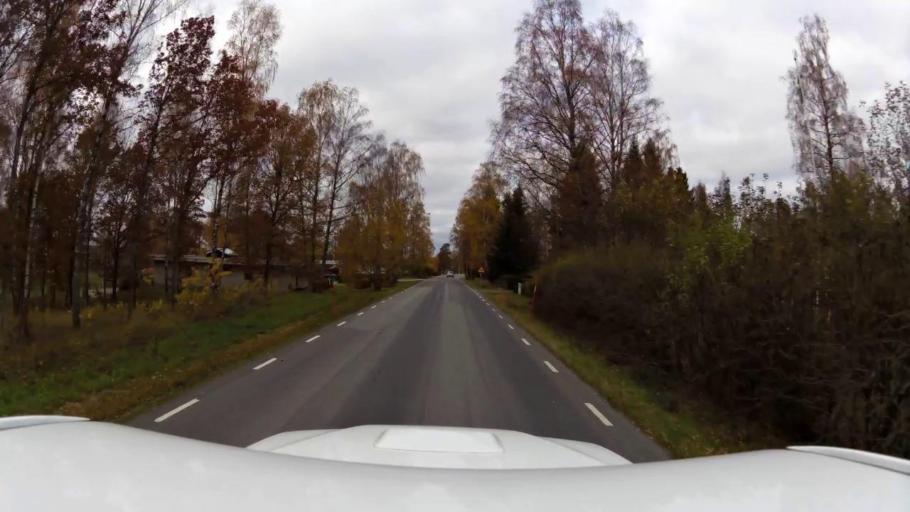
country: SE
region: OEstergoetland
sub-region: Linkopings Kommun
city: Linghem
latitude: 58.4106
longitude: 15.7571
